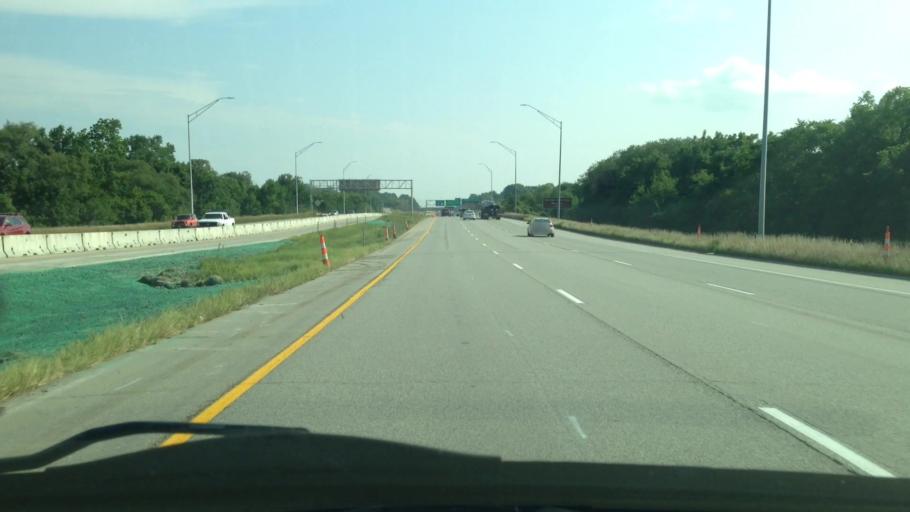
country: US
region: Iowa
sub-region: Linn County
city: Cedar Rapids
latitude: 41.9650
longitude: -91.6708
